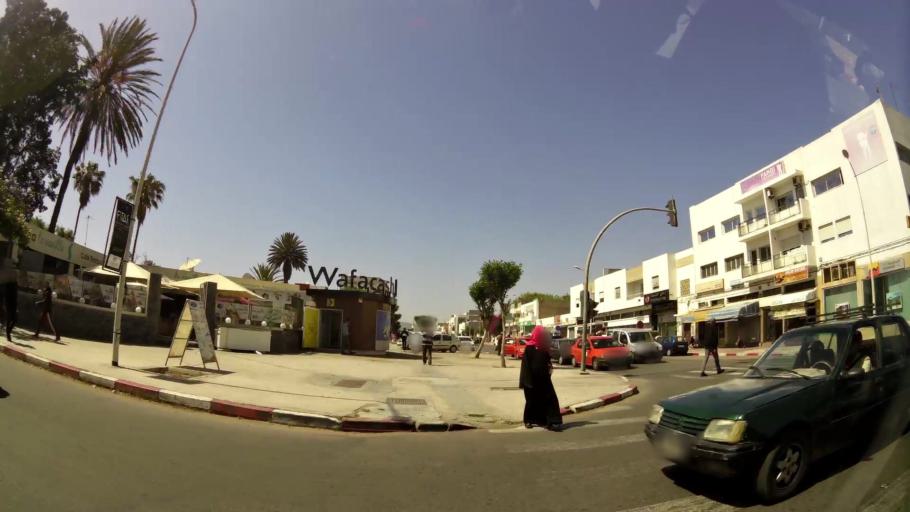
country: MA
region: Souss-Massa-Draa
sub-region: Agadir-Ida-ou-Tnan
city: Agadir
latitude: 30.4133
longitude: -9.5877
